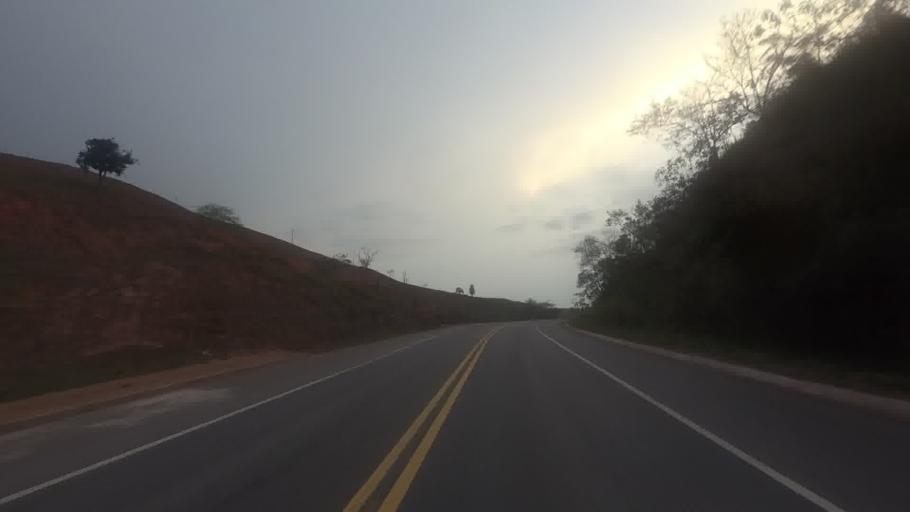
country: BR
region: Minas Gerais
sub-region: Alem Paraiba
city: Alem Paraiba
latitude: -21.8435
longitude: -42.6293
